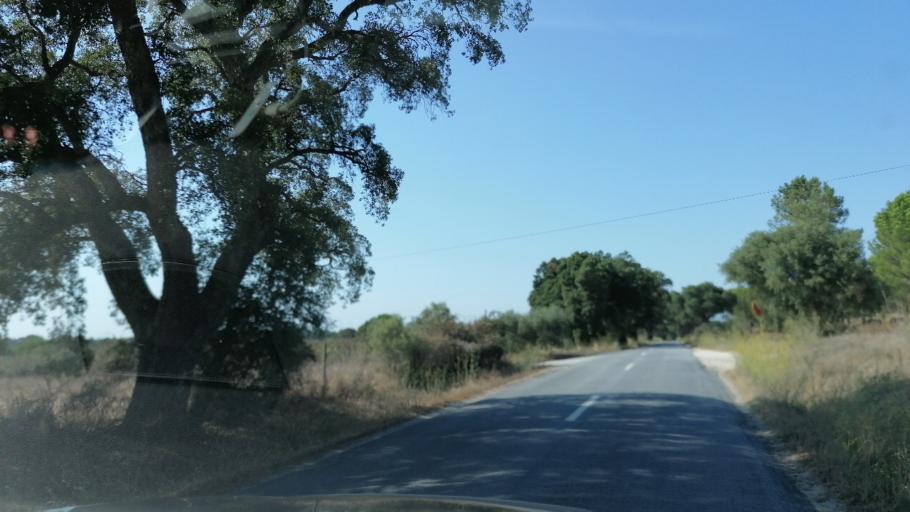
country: PT
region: Santarem
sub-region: Benavente
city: Poceirao
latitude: 38.7534
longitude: -8.6319
